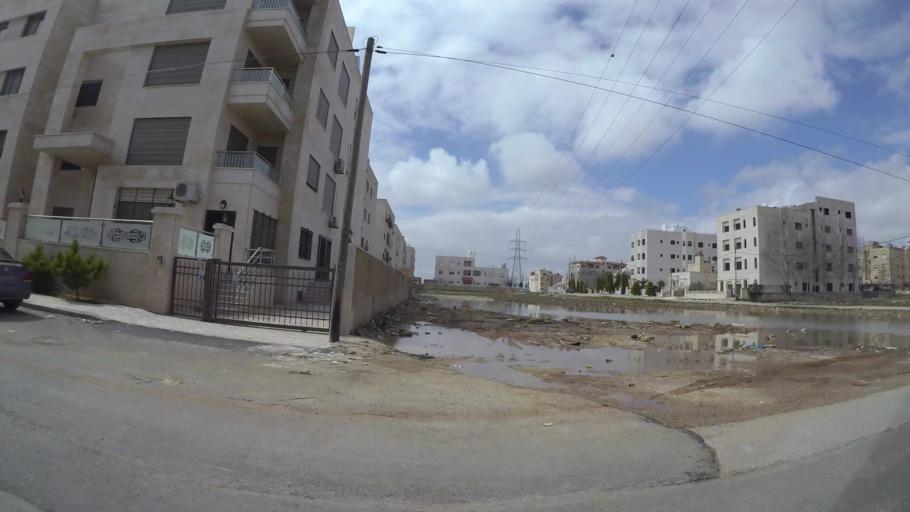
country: JO
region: Amman
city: Wadi as Sir
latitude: 31.9627
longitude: 35.8384
